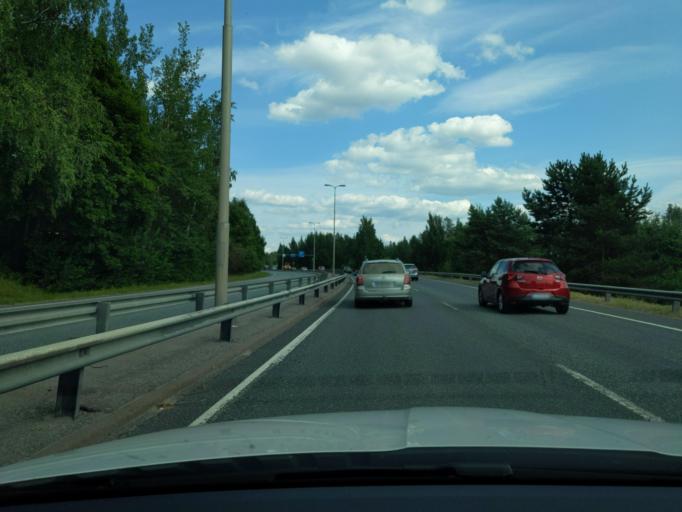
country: FI
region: Paijanne Tavastia
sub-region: Lahti
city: Lahti
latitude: 60.9733
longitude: 25.6975
